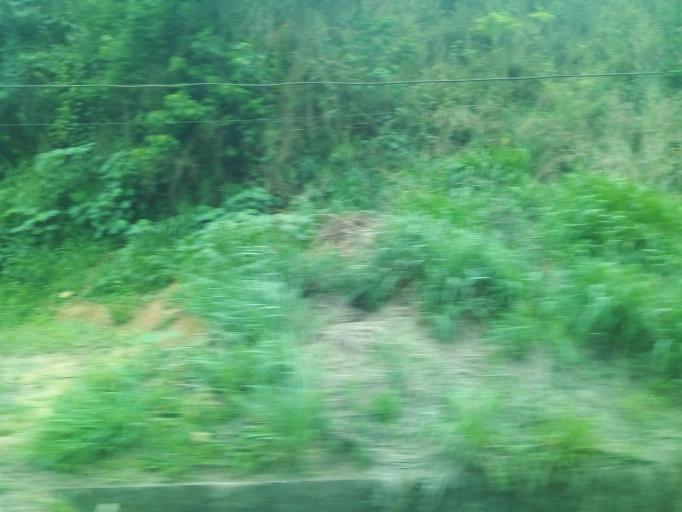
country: BR
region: Minas Gerais
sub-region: Nova Era
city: Nova Era
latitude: -19.7320
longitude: -43.0036
